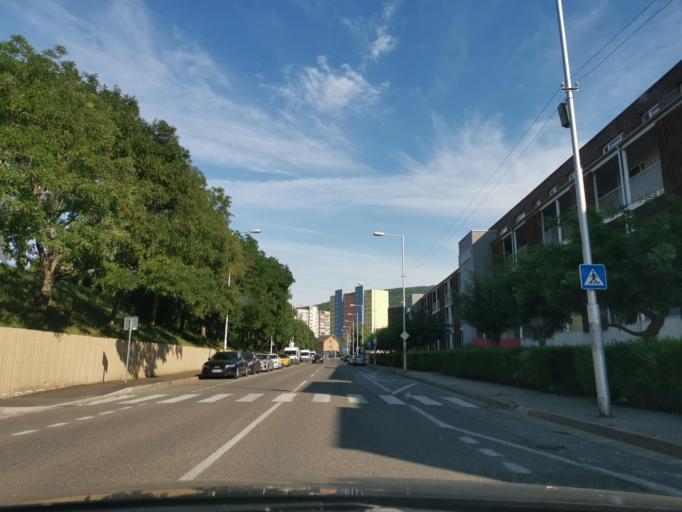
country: AT
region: Lower Austria
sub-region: Politischer Bezirk Bruck an der Leitha
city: Hainburg an der Donau
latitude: 48.2071
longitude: 16.9741
